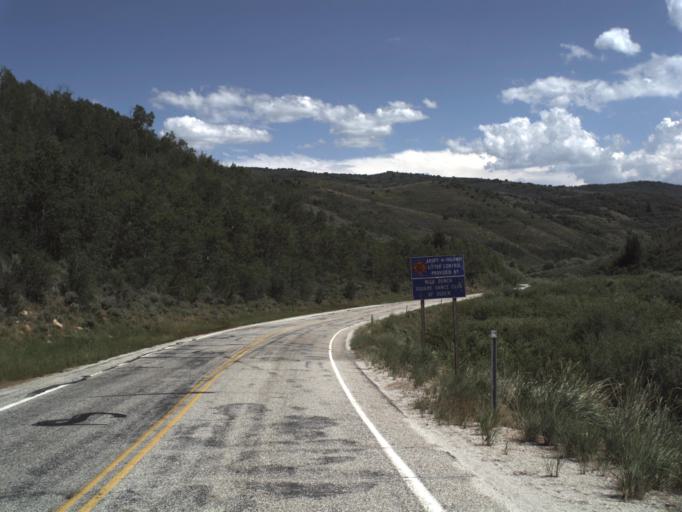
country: US
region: Utah
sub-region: Weber County
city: Wolf Creek
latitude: 41.3876
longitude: -111.5956
